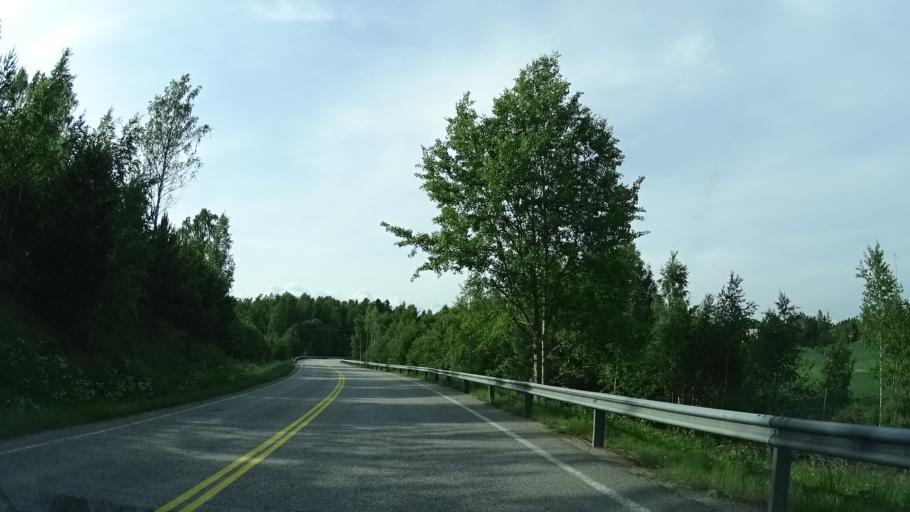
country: FI
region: Uusimaa
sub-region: Helsinki
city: Kirkkonummi
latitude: 60.1121
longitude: 24.4836
